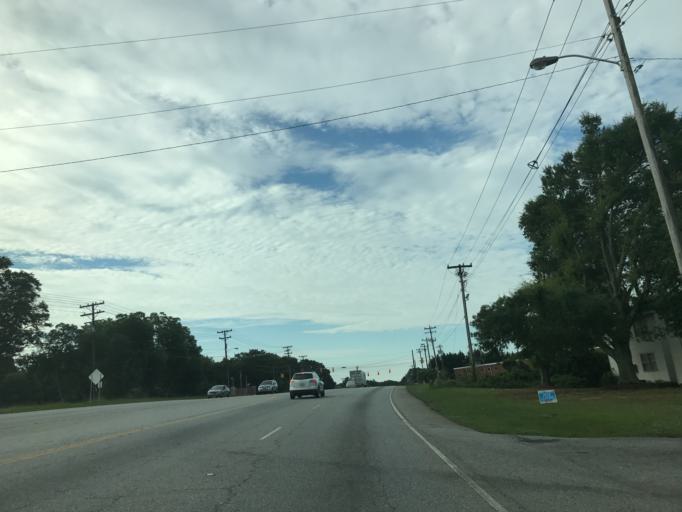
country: US
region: South Carolina
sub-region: Greenville County
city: Mauldin
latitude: 34.8011
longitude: -82.3171
